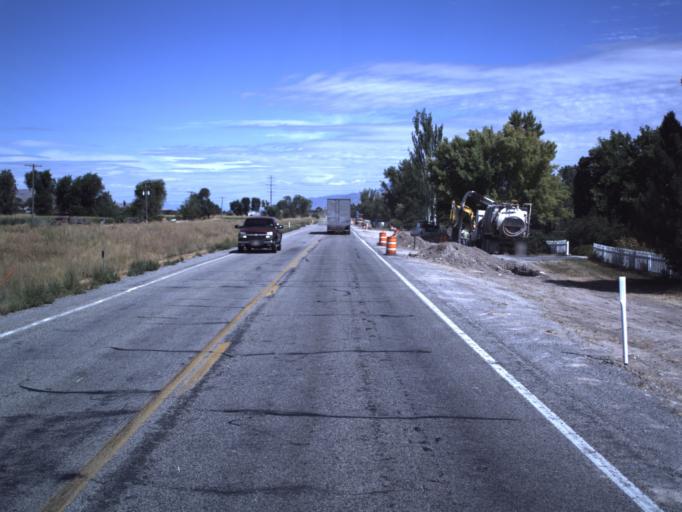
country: US
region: Utah
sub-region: Box Elder County
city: Elwood
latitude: 41.6701
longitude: -112.1409
